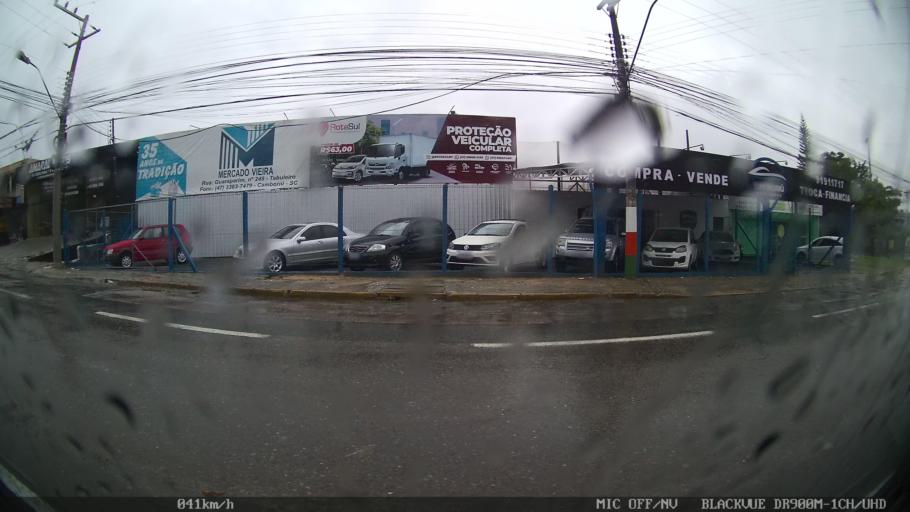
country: BR
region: Santa Catarina
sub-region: Balneario Camboriu
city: Balneario Camboriu
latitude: -27.0145
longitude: -48.6525
